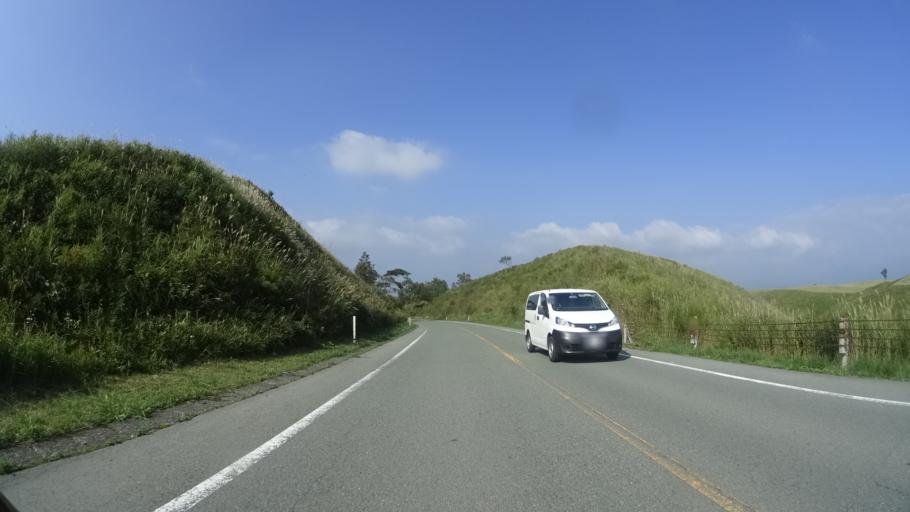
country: JP
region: Kumamoto
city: Aso
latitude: 33.0230
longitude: 131.0680
